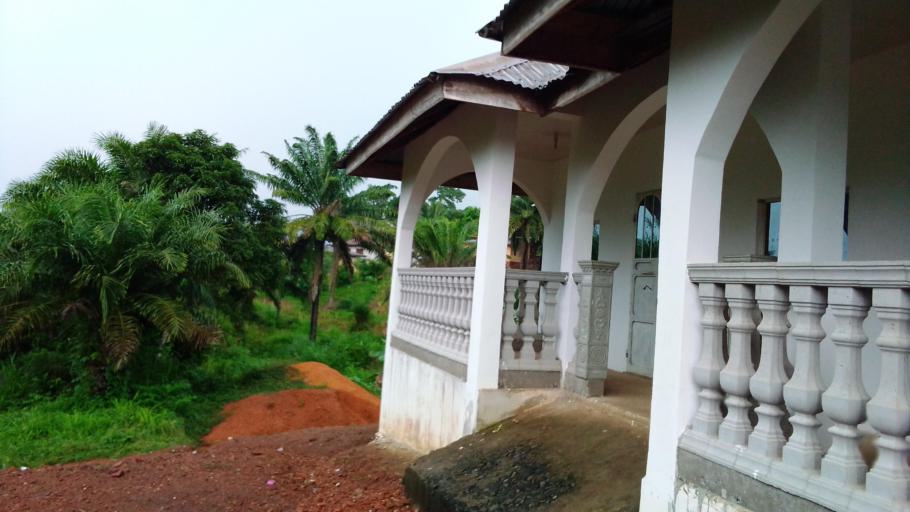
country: SL
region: Eastern Province
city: Kenema
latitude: 7.8793
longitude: -11.1715
